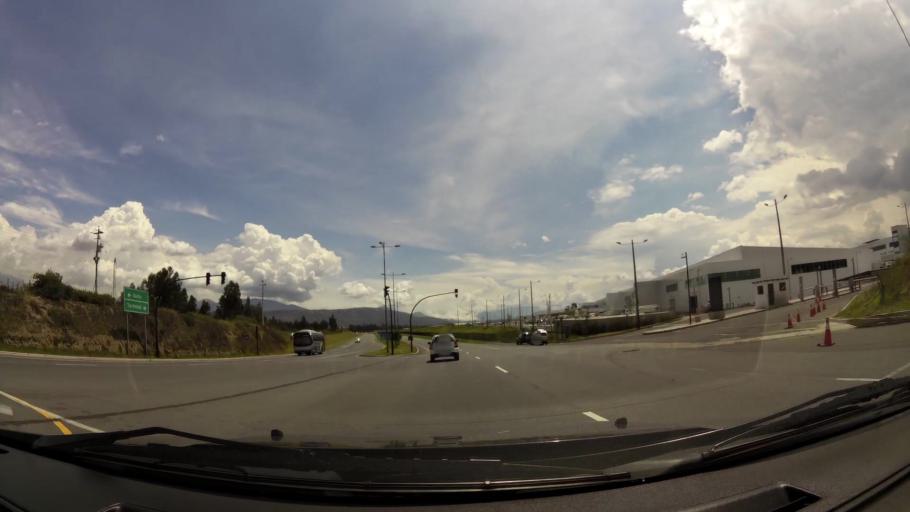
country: EC
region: Pichincha
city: Quito
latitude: -0.1541
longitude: -78.3498
